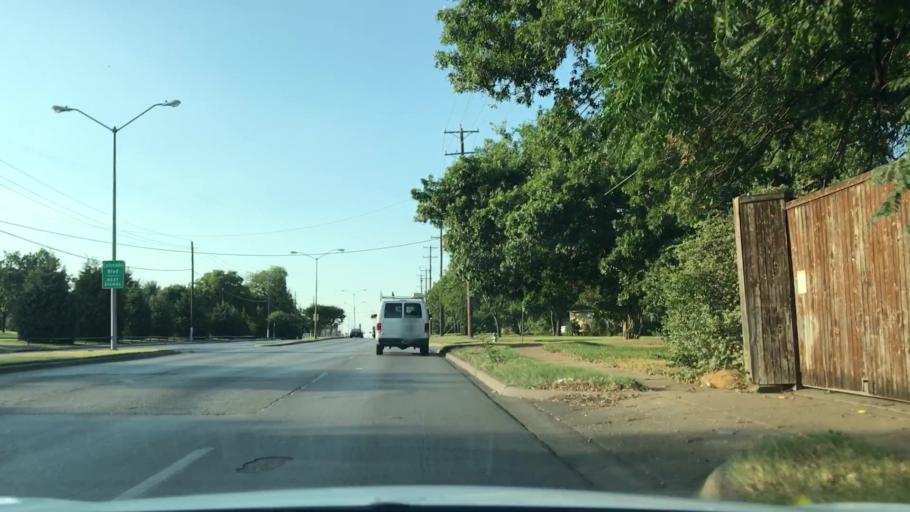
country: US
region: Texas
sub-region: Dallas County
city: Cockrell Hill
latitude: 32.7579
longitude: -96.8566
